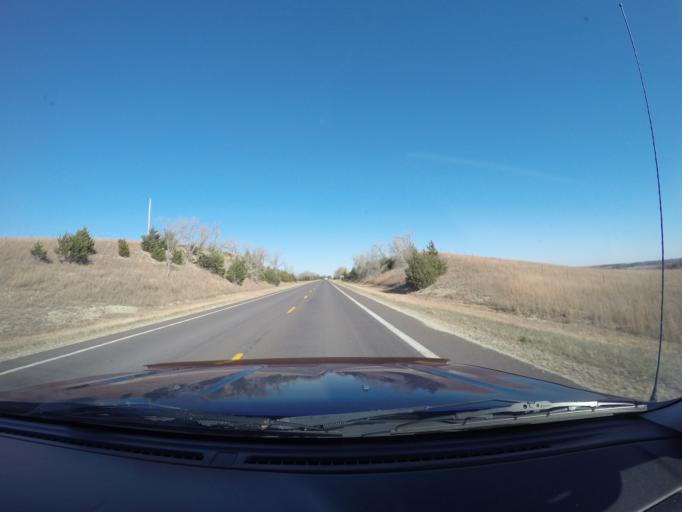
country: US
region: Kansas
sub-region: Marshall County
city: Blue Rapids
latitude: 39.4466
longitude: -96.7642
